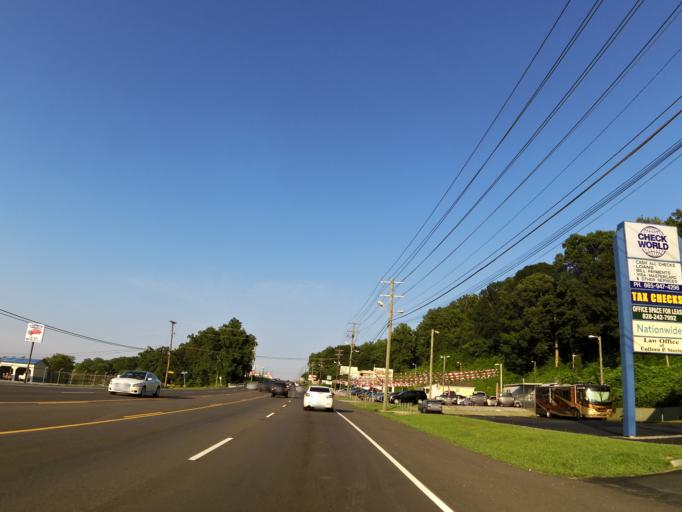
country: US
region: Tennessee
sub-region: Knox County
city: Knoxville
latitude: 36.0069
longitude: -84.0162
